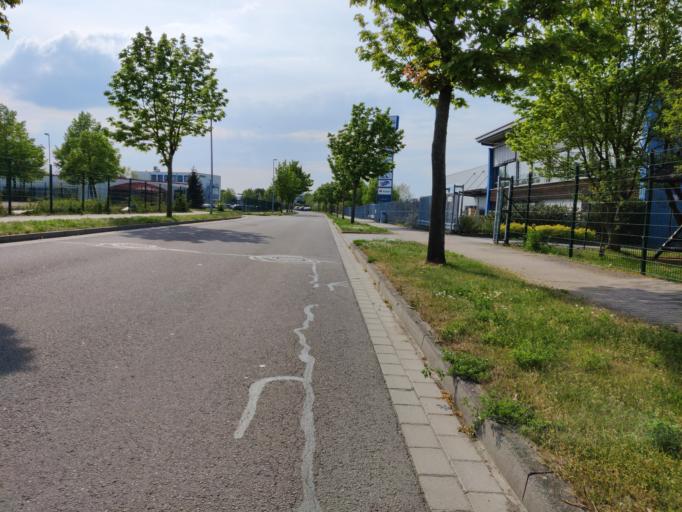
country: DE
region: Saxony
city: Zwenkau
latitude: 51.2114
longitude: 12.3380
